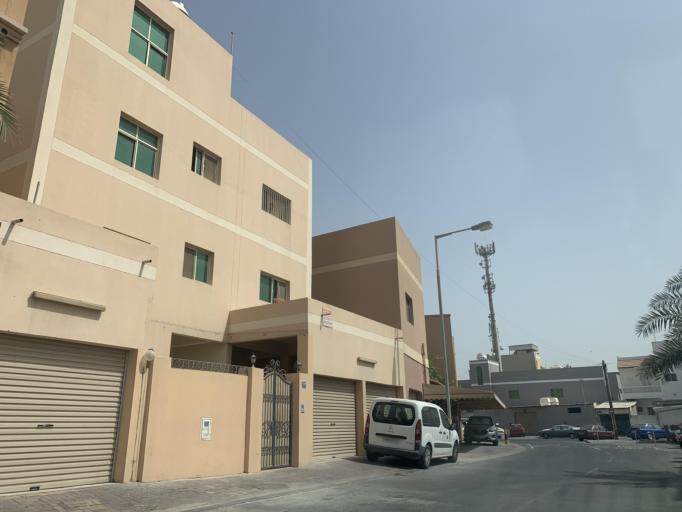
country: BH
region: Northern
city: Madinat `Isa
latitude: 26.1807
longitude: 50.5256
